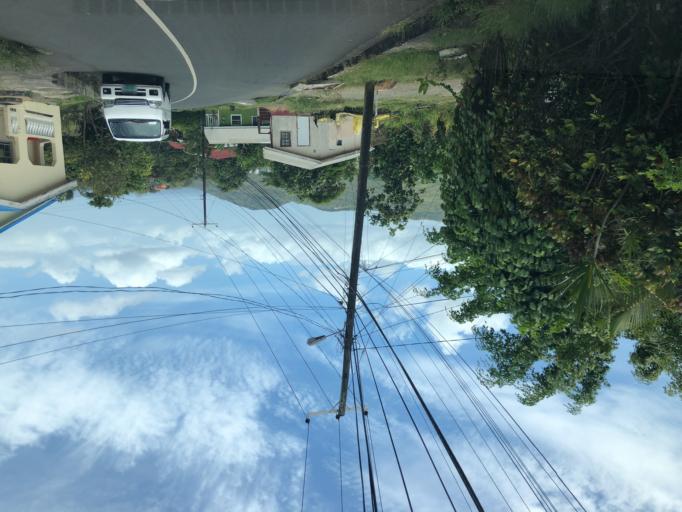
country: LC
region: Castries Quarter
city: Castries
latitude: 13.9964
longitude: -61.0032
